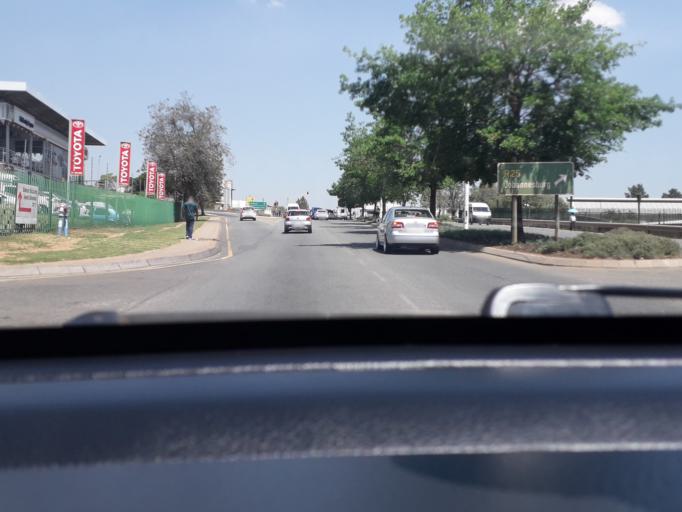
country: ZA
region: Gauteng
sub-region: City of Johannesburg Metropolitan Municipality
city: Modderfontein
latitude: -26.1174
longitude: 28.1372
